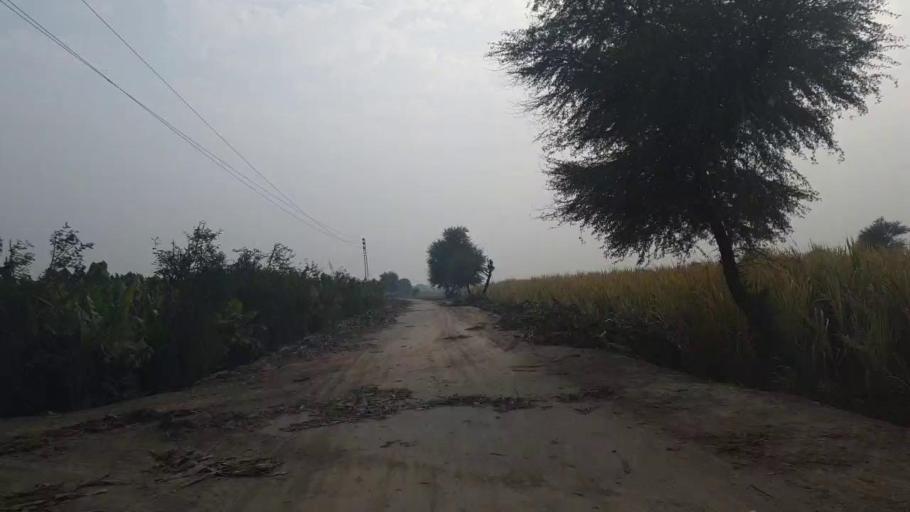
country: PK
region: Sindh
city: Berani
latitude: 25.8047
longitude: 68.7326
